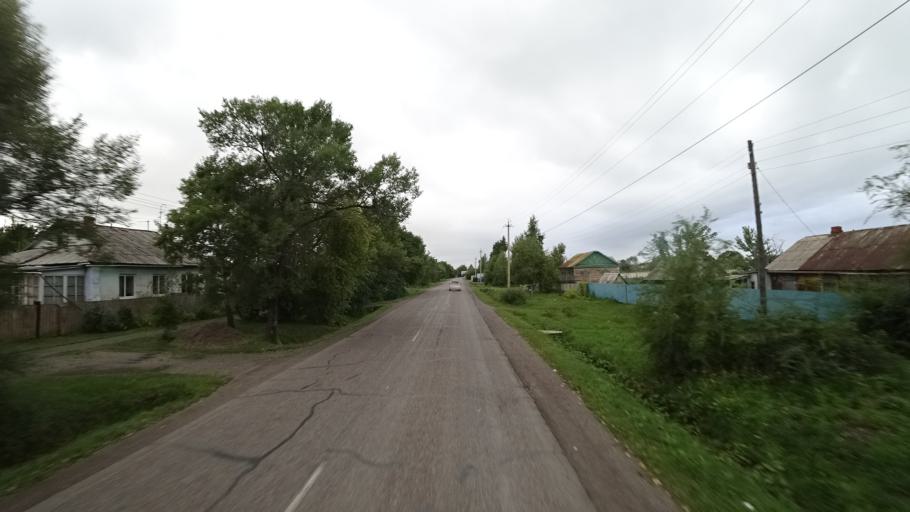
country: RU
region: Primorskiy
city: Chernigovka
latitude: 44.3484
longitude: 132.5711
